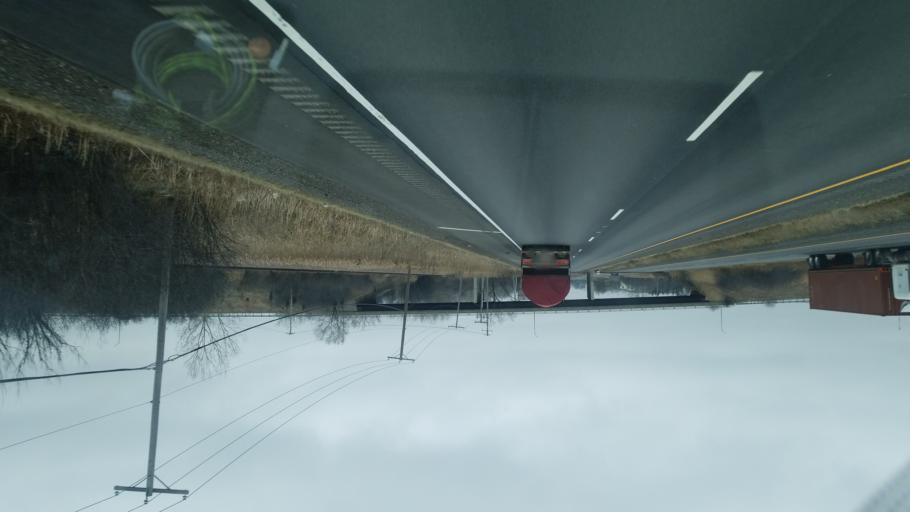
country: US
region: Illinois
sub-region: Lake County
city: Park City
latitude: 42.3326
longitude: -87.8842
